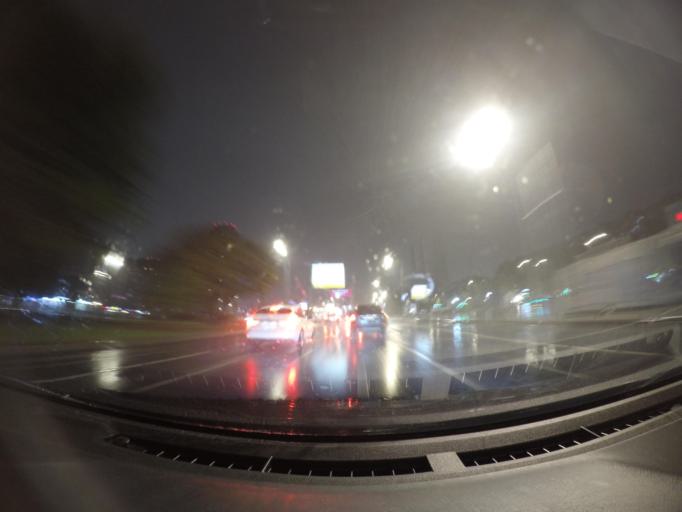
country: RU
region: Moskovskaya
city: Kozhukhovo
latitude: 55.6794
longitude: 37.6646
